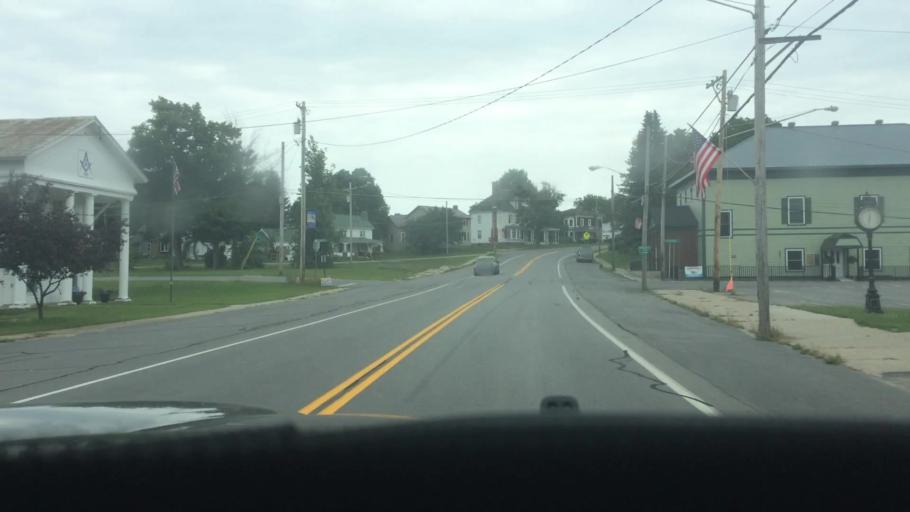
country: US
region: New York
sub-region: St. Lawrence County
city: Hannawa Falls
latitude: 44.6283
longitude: -74.8144
